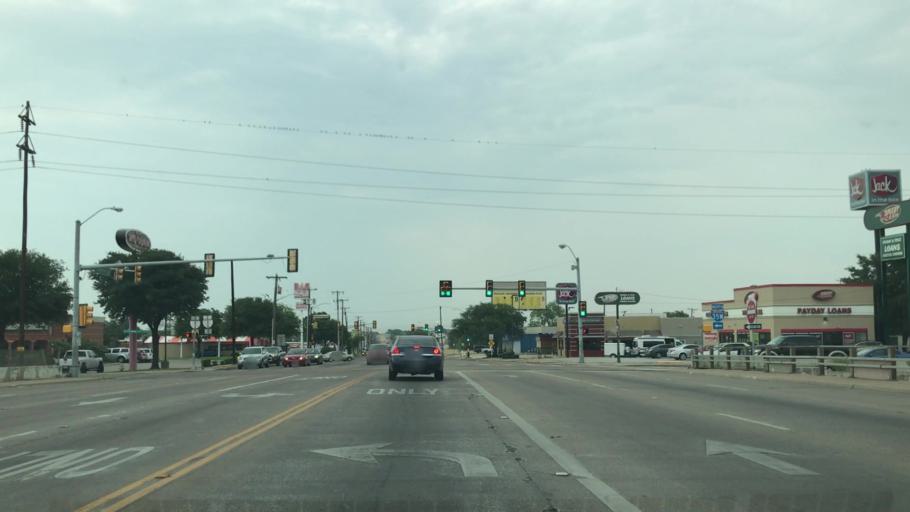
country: US
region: Texas
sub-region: Tarrant County
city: Edgecliff Village
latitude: 32.6843
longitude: -97.3208
